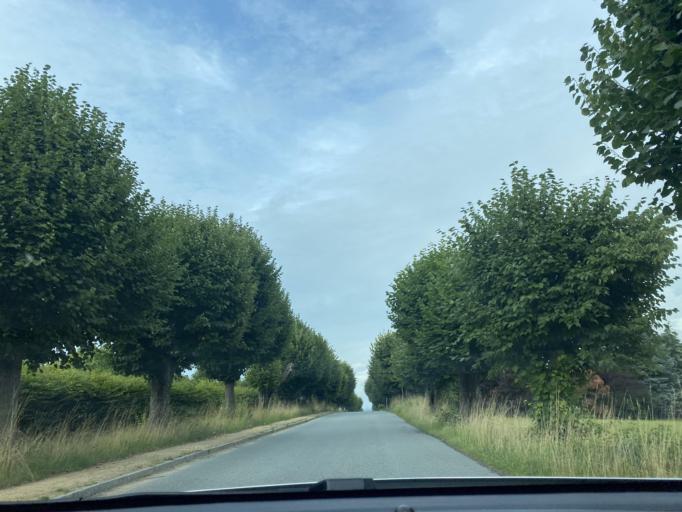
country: DE
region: Saxony
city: Herrnhut
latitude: 51.0184
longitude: 14.7499
